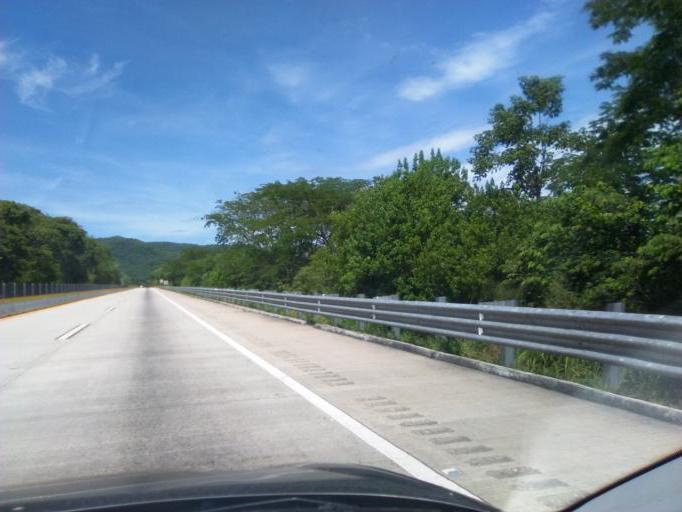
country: MX
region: Guerrero
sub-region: Acapulco de Juarez
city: Pueblo Madero (El Playon)
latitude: 17.0542
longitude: -99.6308
